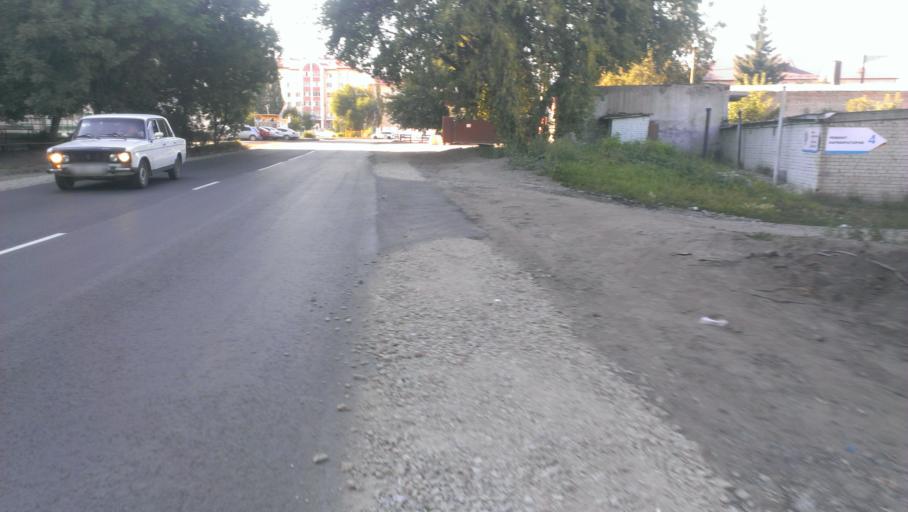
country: RU
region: Altai Krai
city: Novosilikatnyy
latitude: 53.3071
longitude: 83.6236
